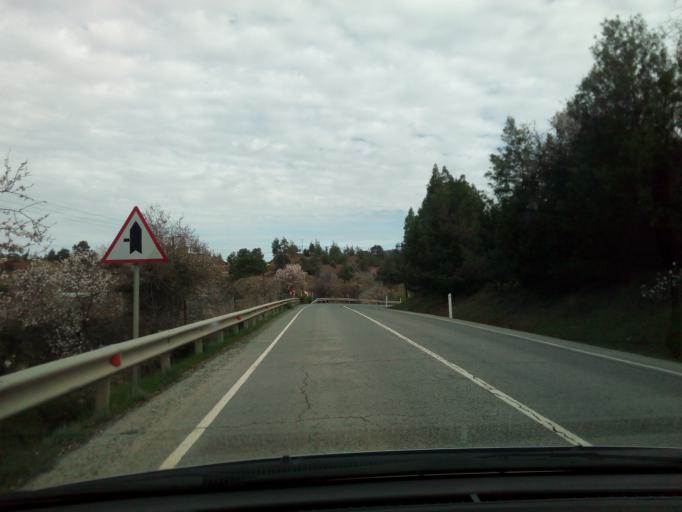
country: CY
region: Lefkosia
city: Klirou
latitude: 34.9831
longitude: 33.1581
